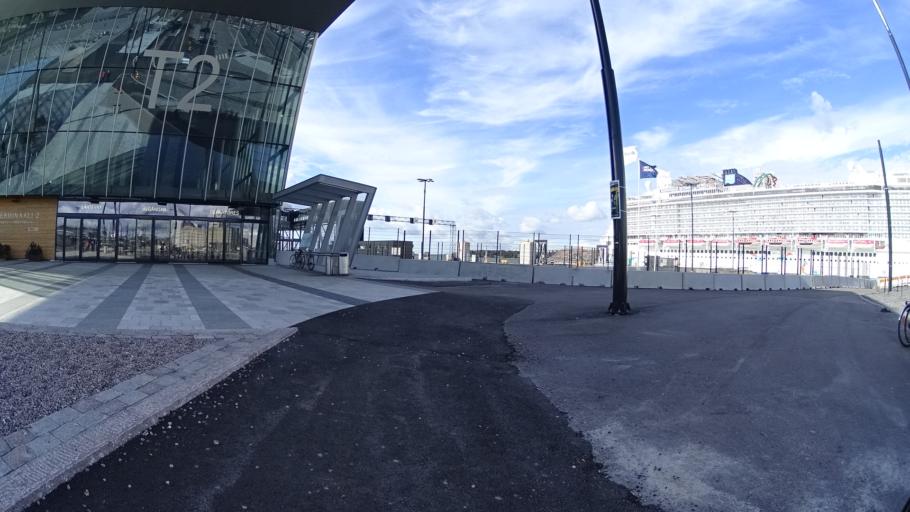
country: FI
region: Uusimaa
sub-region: Helsinki
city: Helsinki
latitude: 60.1505
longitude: 24.9154
